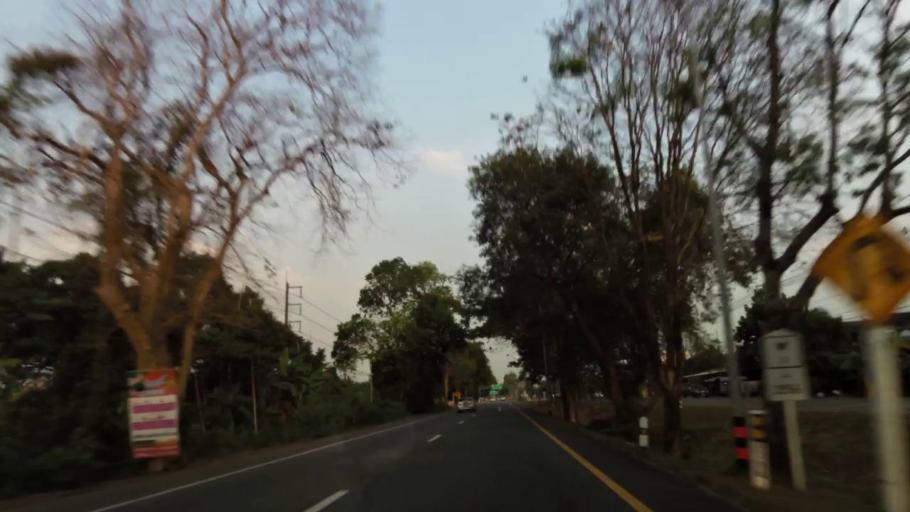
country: TH
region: Chanthaburi
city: Khlung
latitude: 12.4654
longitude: 102.2148
